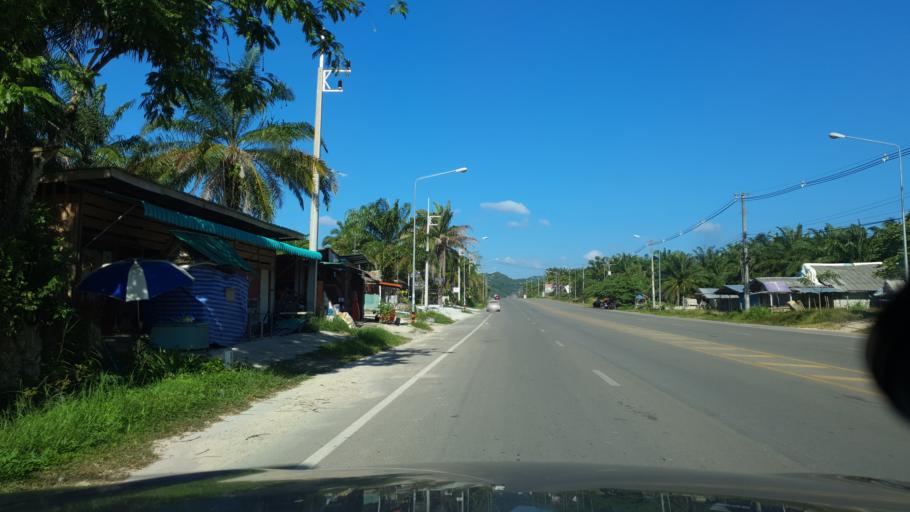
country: TH
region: Phangnga
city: Ban Ao Nang
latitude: 8.0359
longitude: 98.8564
